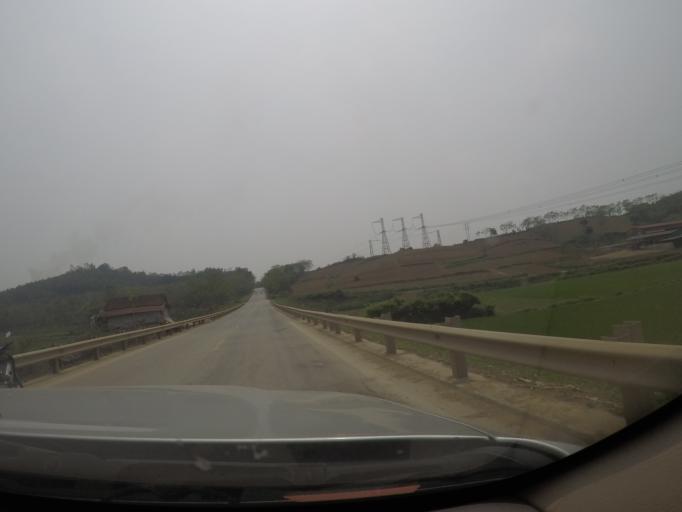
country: VN
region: Thanh Hoa
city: Thi Tran Thuong Xuan
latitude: 19.9034
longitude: 105.3982
